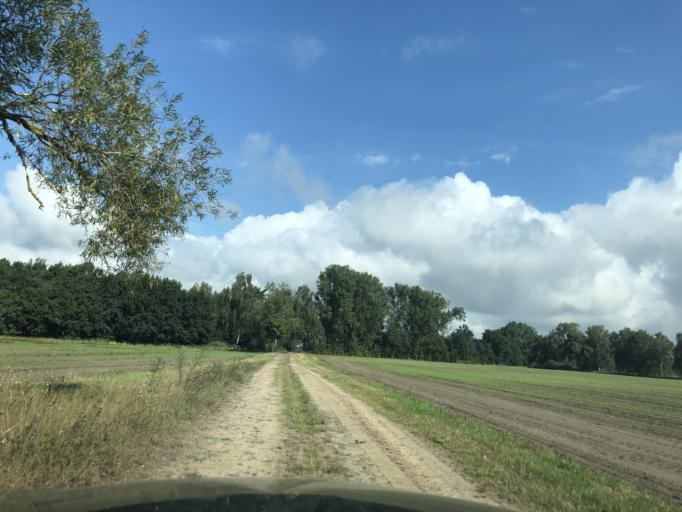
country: DE
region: Brandenburg
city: Schlepzig
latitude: 52.0140
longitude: 13.9597
